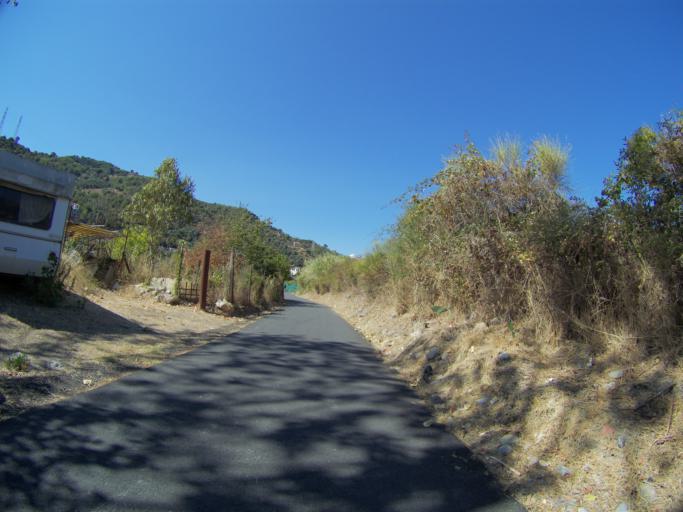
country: IT
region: Liguria
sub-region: Provincia di Imperia
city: Camporosso
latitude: 43.8225
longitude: 7.6306
